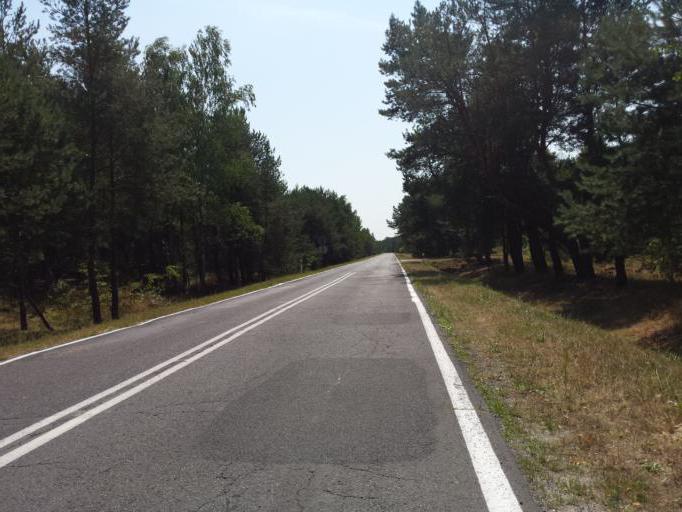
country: PL
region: Lublin Voivodeship
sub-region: Powiat bialski
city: Koden
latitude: 51.8943
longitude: 23.5974
